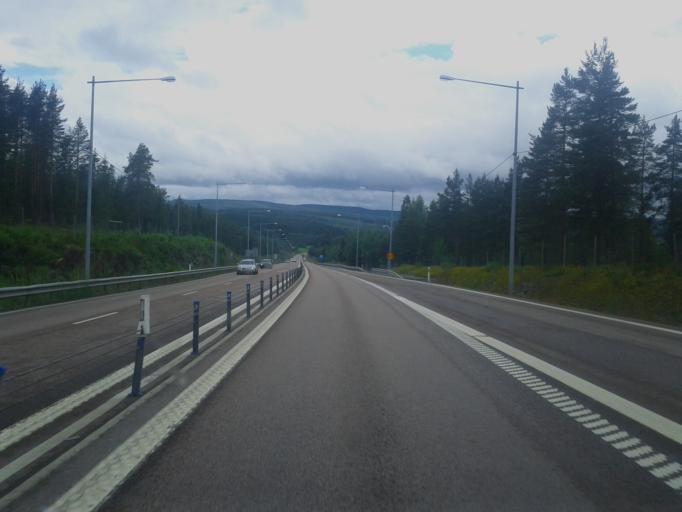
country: SE
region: Vaesternorrland
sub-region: Haernoesands Kommun
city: Haernoesand
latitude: 62.6548
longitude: 17.8806
